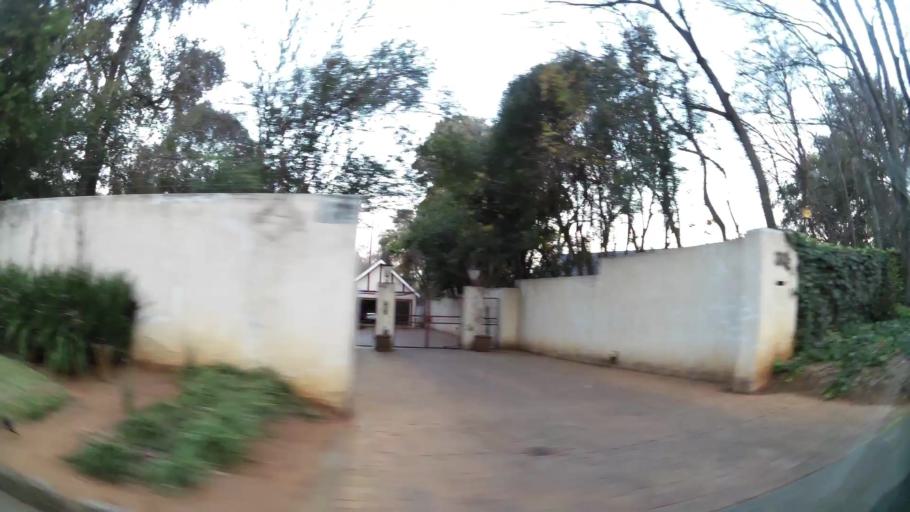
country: ZA
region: Gauteng
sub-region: City of Johannesburg Metropolitan Municipality
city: Johannesburg
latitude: -26.1405
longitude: 28.0576
